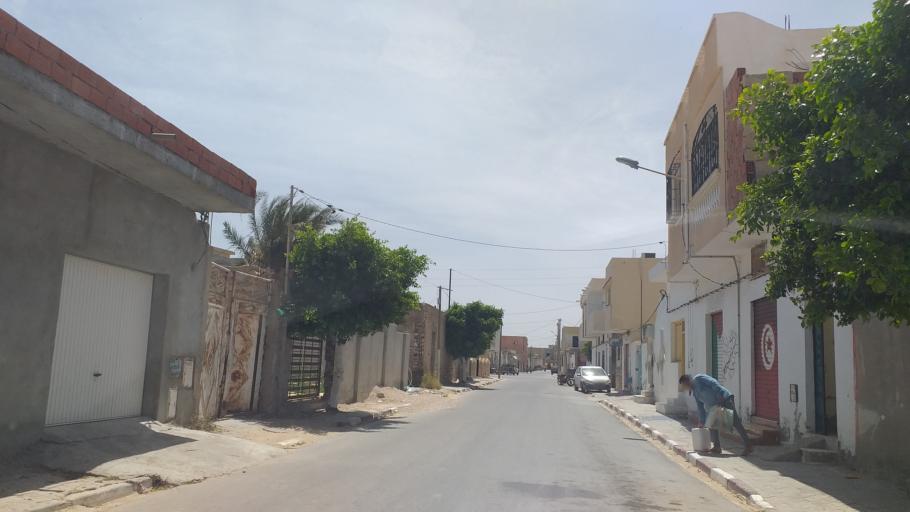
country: TN
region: Qabis
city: Gabes
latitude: 33.9395
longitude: 10.0614
